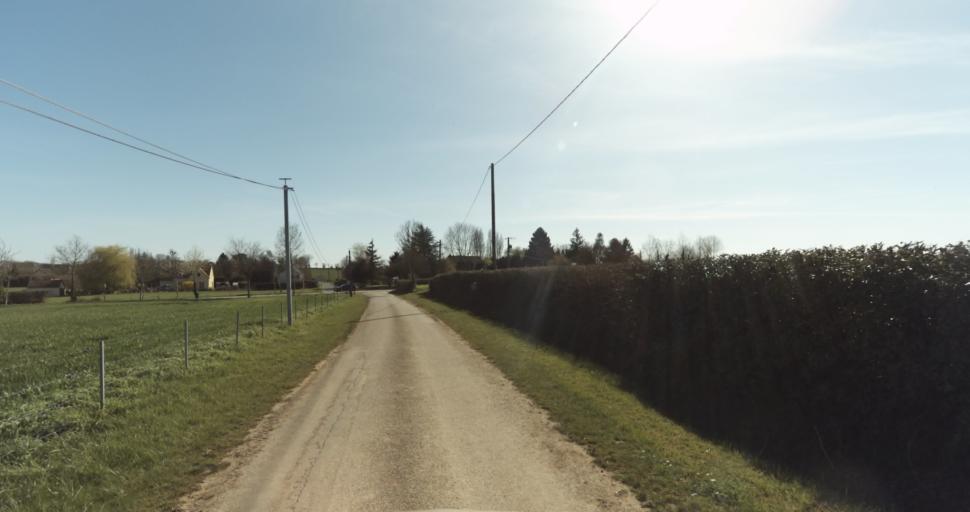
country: FR
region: Lower Normandy
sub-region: Departement du Calvados
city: Saint-Pierre-sur-Dives
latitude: 49.0166
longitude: 0.0142
